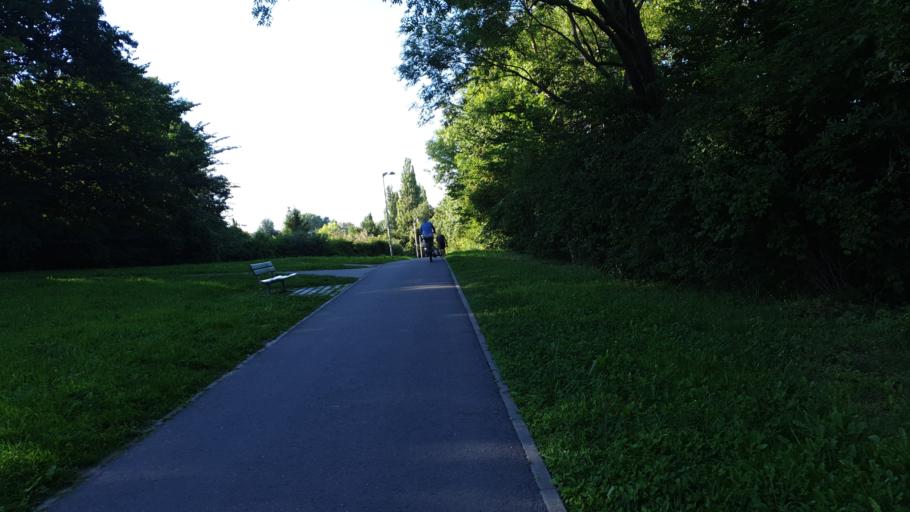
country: DE
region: Mecklenburg-Vorpommern
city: Stralsund
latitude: 54.3330
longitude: 13.0803
